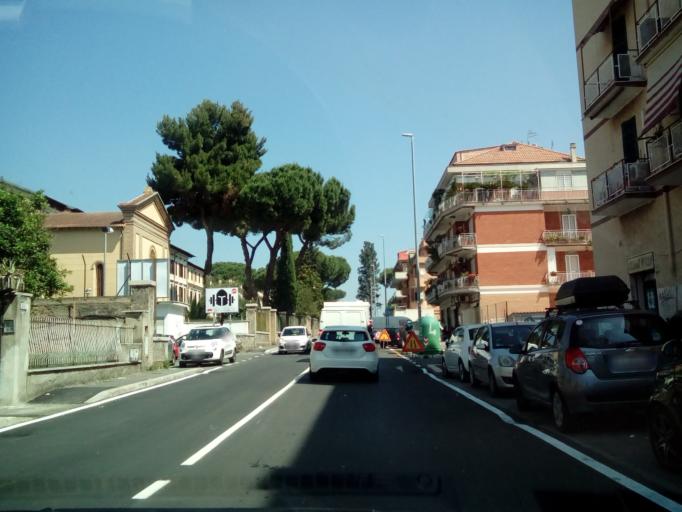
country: IT
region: Latium
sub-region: Citta metropolitana di Roma Capitale
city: Rome
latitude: 41.8857
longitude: 12.5769
